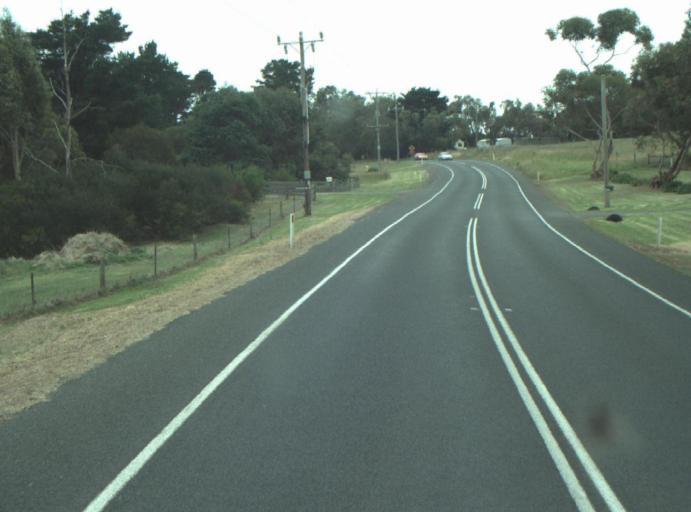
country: AU
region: Victoria
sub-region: Greater Geelong
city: Leopold
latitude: -38.2123
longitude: 144.5075
